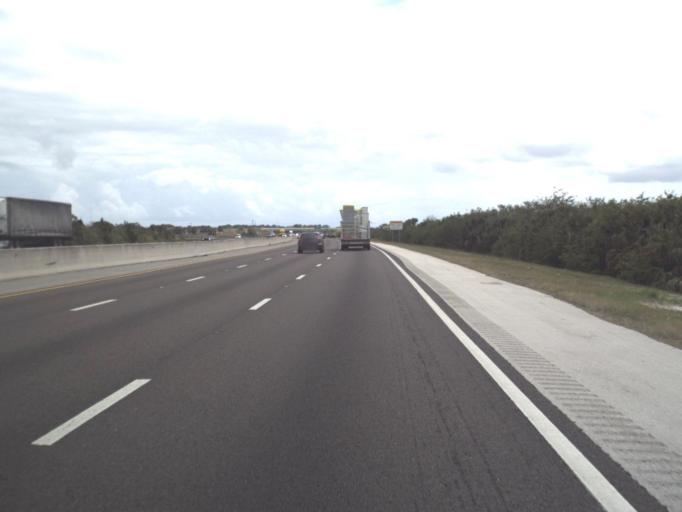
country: US
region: Florida
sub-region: Brevard County
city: Rockledge
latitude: 28.2974
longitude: -80.7510
